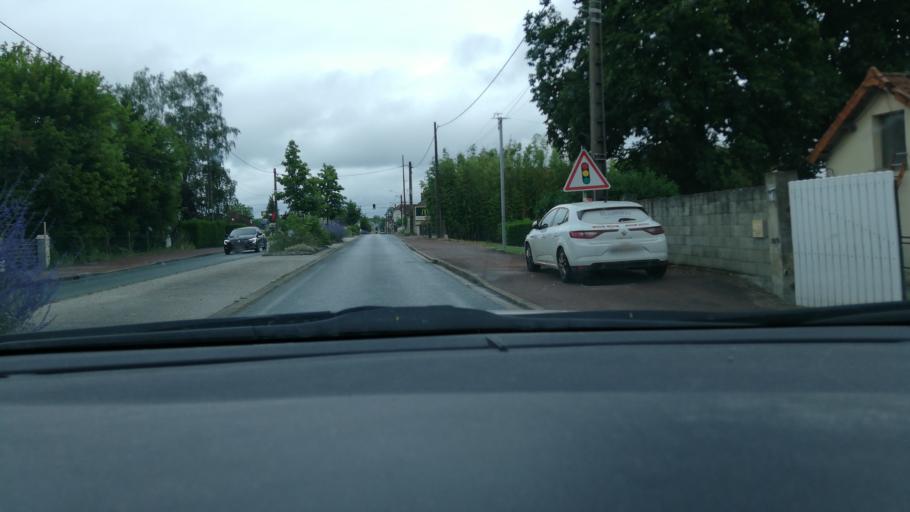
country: FR
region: Poitou-Charentes
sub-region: Departement de la Vienne
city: Naintre
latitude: 46.7603
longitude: 0.4913
